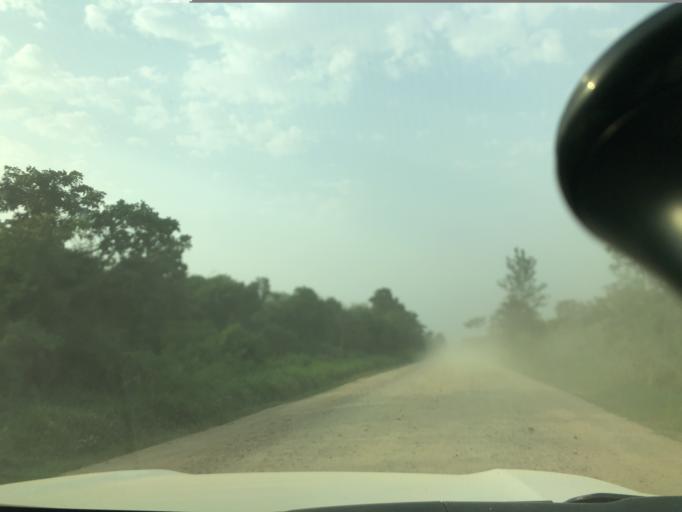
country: UG
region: Western Region
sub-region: Kasese District
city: Margherita
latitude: 0.2694
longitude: 29.6748
